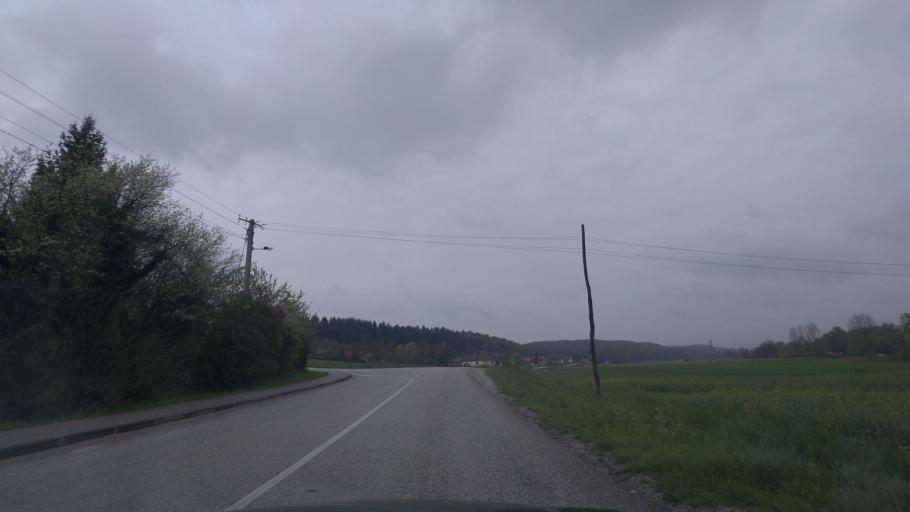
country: HR
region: Zagrebacka
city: Jastrebarsko
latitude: 45.6203
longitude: 15.5691
